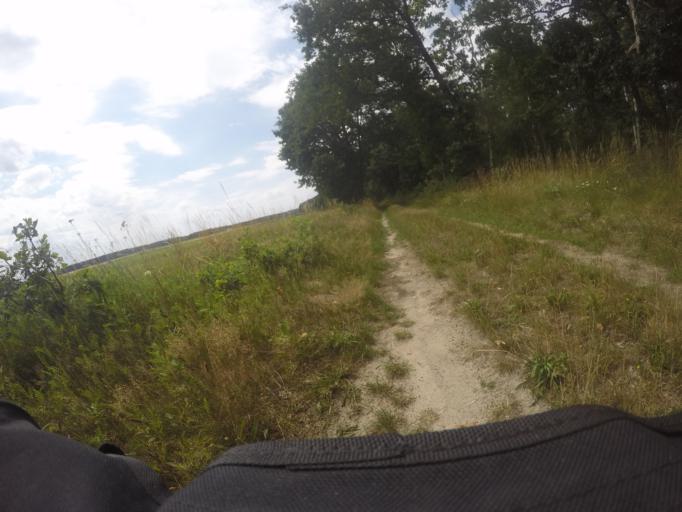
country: DE
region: Lower Saxony
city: Dahlem
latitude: 53.2356
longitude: 10.7517
